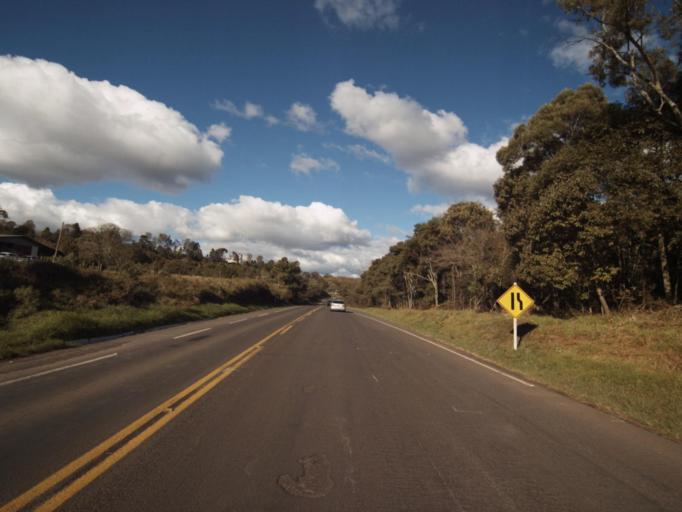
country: BR
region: Santa Catarina
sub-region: Joacaba
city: Joacaba
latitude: -27.1651
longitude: -51.5652
